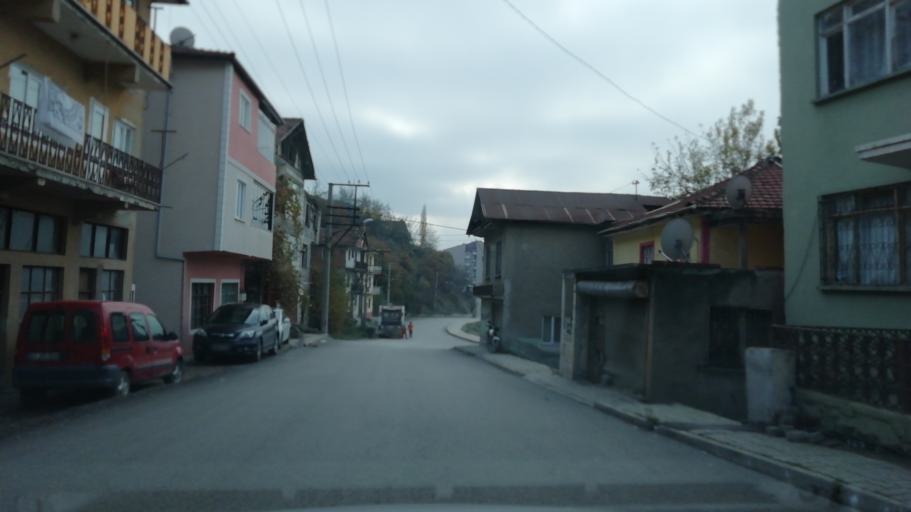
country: TR
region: Karabuk
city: Karabuk
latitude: 41.2125
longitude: 32.6287
